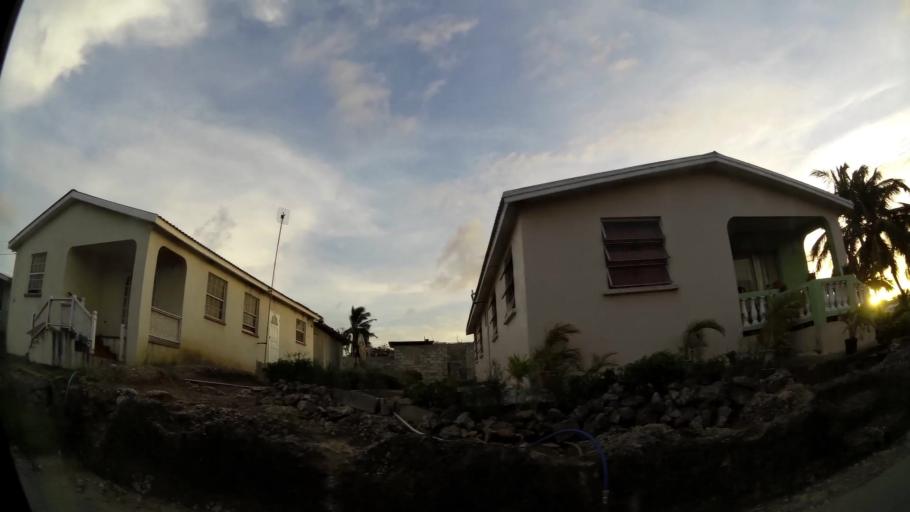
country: BB
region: Saint Philip
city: Crane
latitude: 13.0968
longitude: -59.4926
